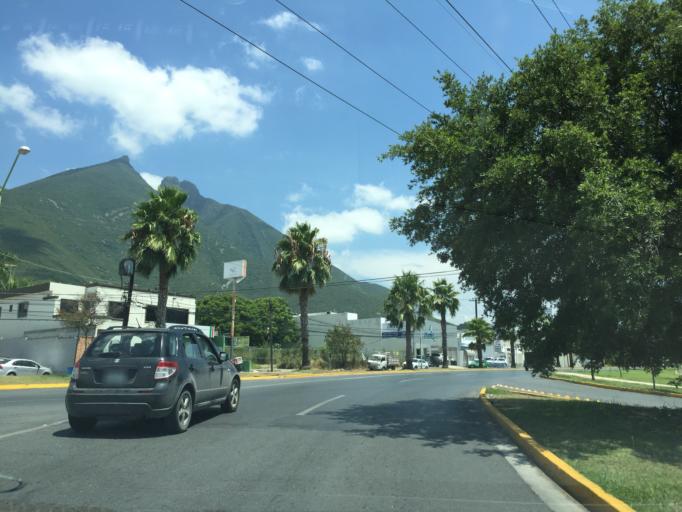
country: MX
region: Nuevo Leon
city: Guadalupe
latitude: 25.6465
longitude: -100.2682
